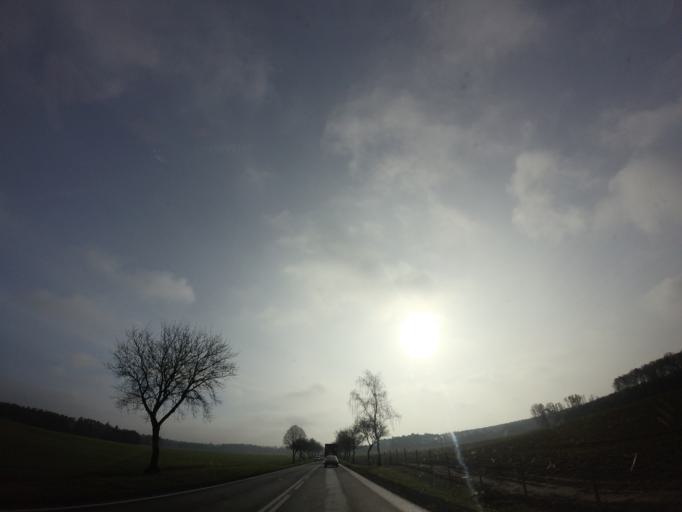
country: PL
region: West Pomeranian Voivodeship
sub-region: Powiat walecki
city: Walcz
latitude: 53.3188
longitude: 16.3260
